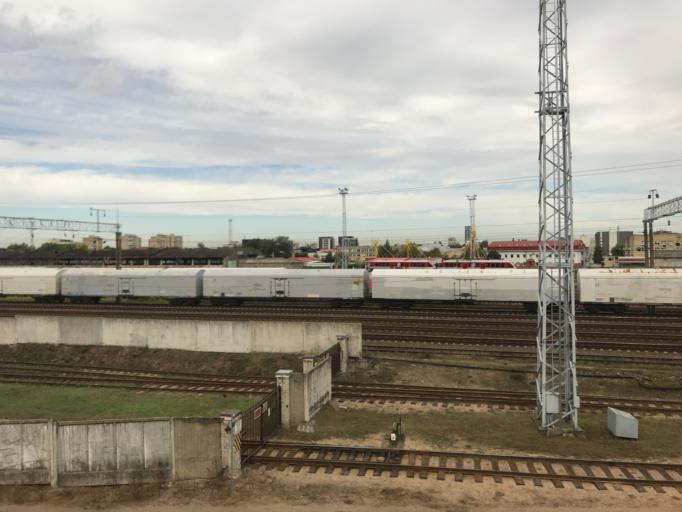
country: LT
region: Vilnius County
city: Naujamiestis
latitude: 54.6658
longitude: 25.2690
